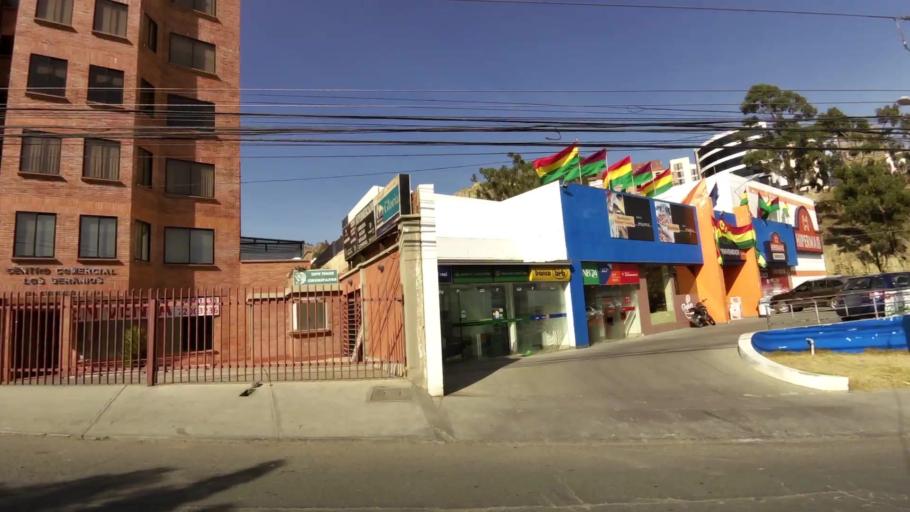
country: BO
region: La Paz
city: La Paz
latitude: -16.5188
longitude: -68.0624
